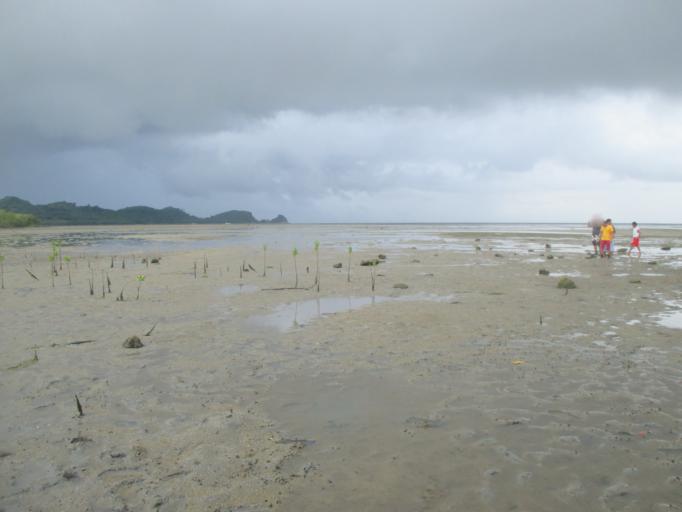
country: PH
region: Calabarzon
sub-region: Province of Batangas
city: Binubusan
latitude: 13.9690
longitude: 120.6244
